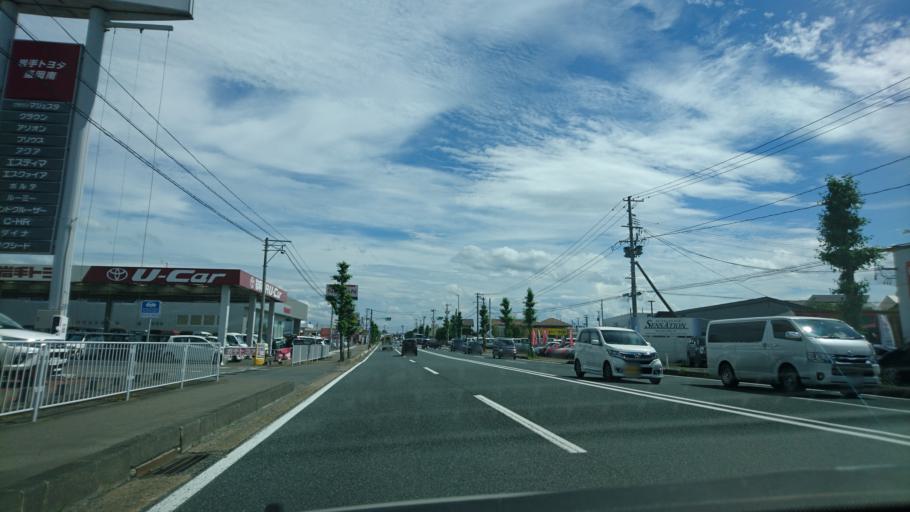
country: JP
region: Iwate
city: Morioka-shi
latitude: 39.6307
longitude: 141.1739
